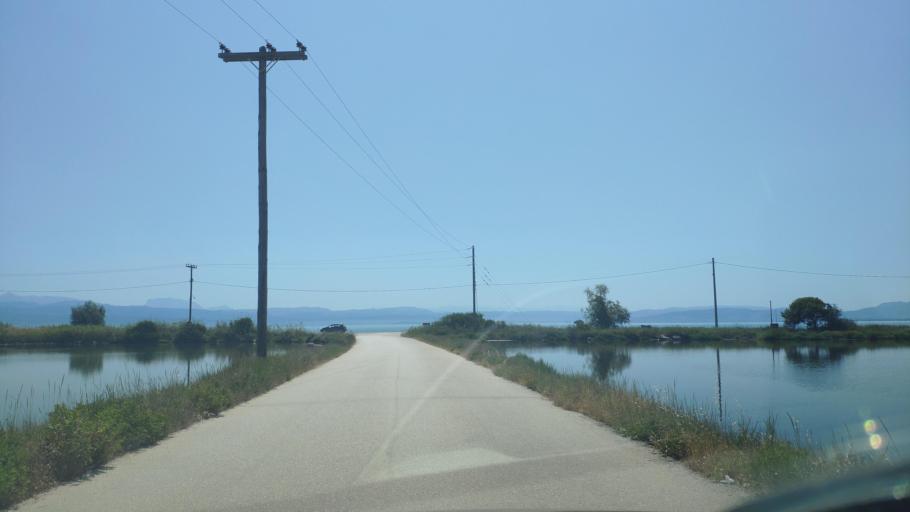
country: GR
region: Epirus
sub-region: Nomos Artas
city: Aneza
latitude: 39.0121
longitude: 20.9246
